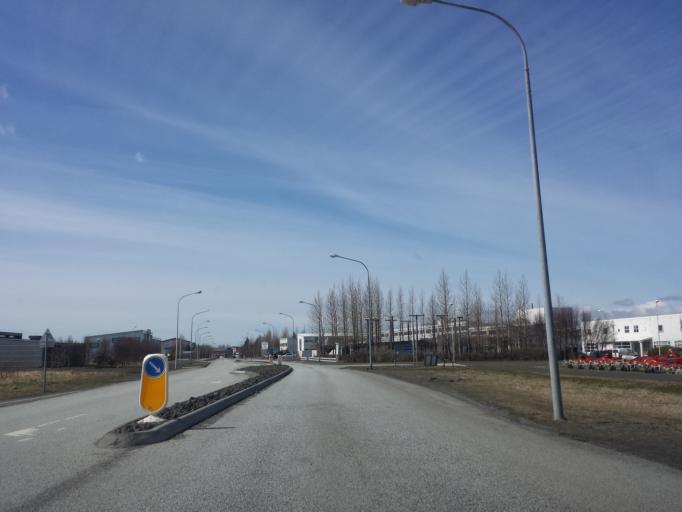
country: IS
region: South
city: Selfoss
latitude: 63.9387
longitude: -20.9768
